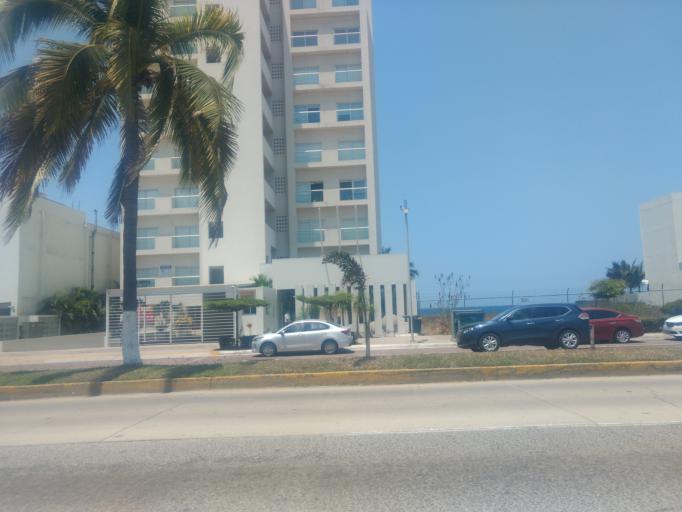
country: MX
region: Colima
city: Tapeixtles
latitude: 19.0881
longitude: -104.3115
